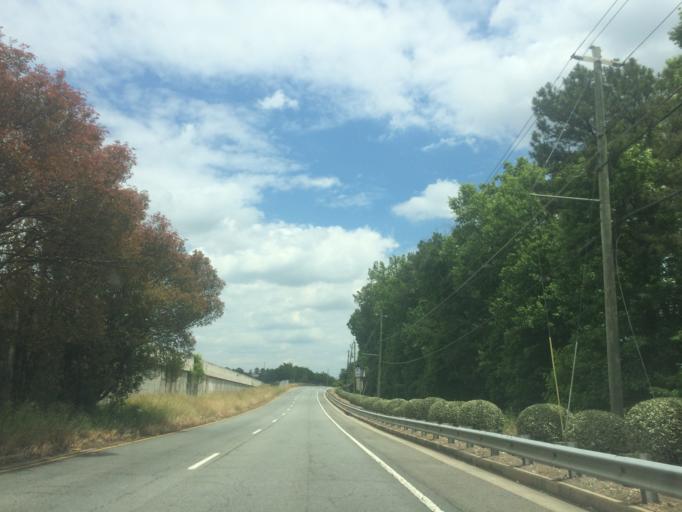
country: US
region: Georgia
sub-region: DeKalb County
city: Chamblee
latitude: 33.8591
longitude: -84.2930
